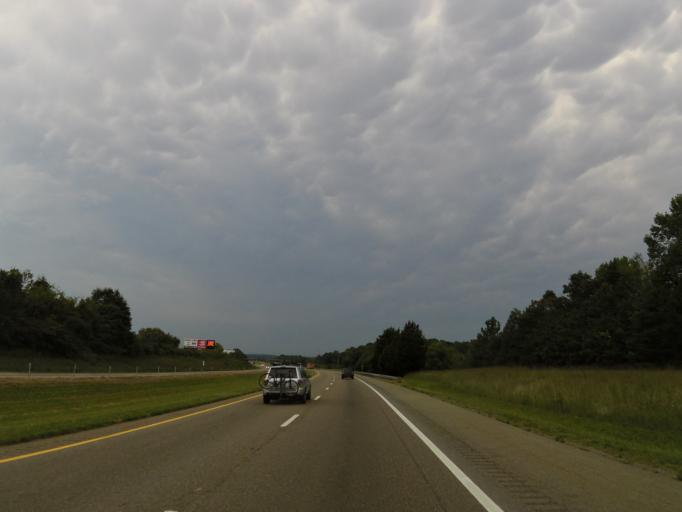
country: US
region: Tennessee
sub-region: Jefferson County
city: White Pine
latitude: 36.0234
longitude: -83.3009
